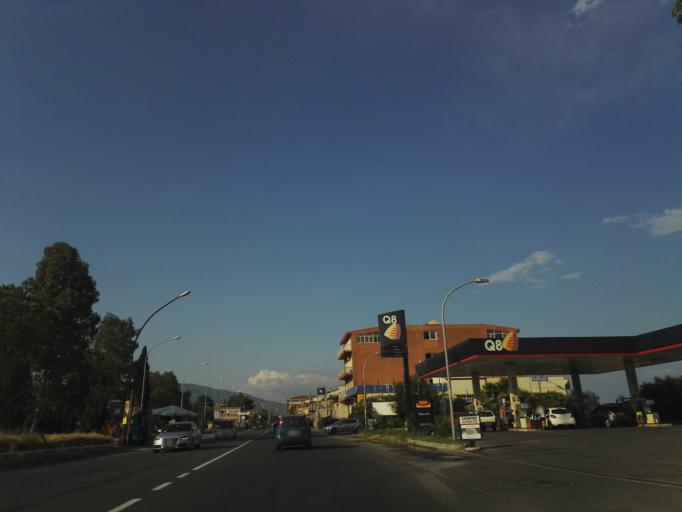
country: IT
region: Calabria
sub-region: Provincia di Reggio Calabria
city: Siderno
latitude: 38.2811
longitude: 16.3109
